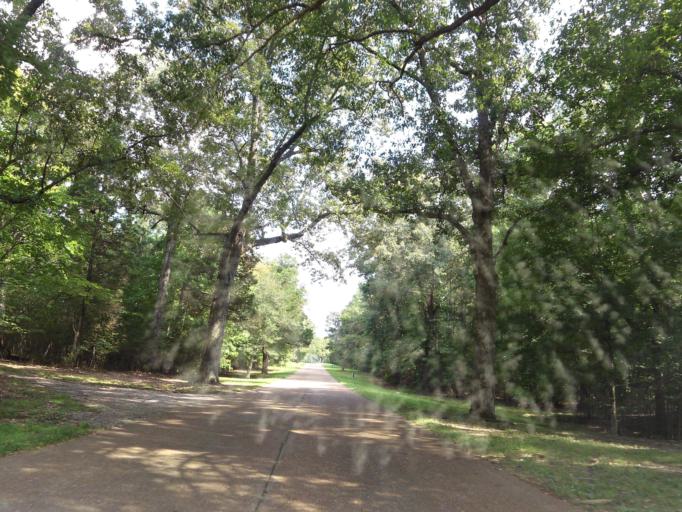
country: US
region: Tennessee
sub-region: Hardin County
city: Crump
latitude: 35.1332
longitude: -88.3445
